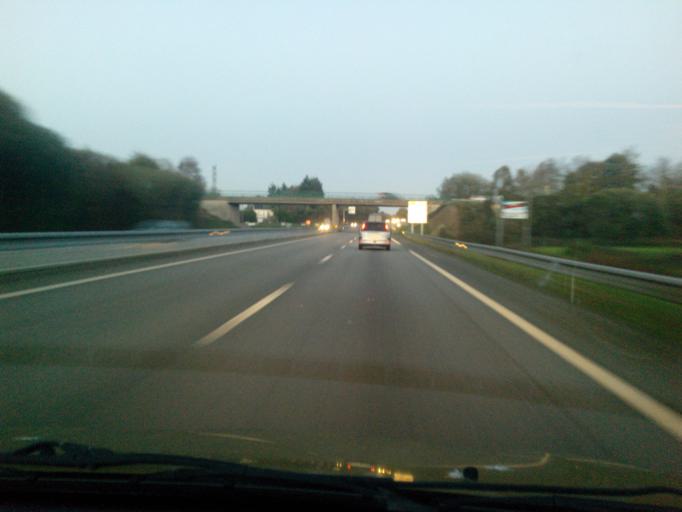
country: FR
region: Brittany
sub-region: Departement du Morbihan
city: Guegon
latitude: 47.9561
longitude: -2.5708
